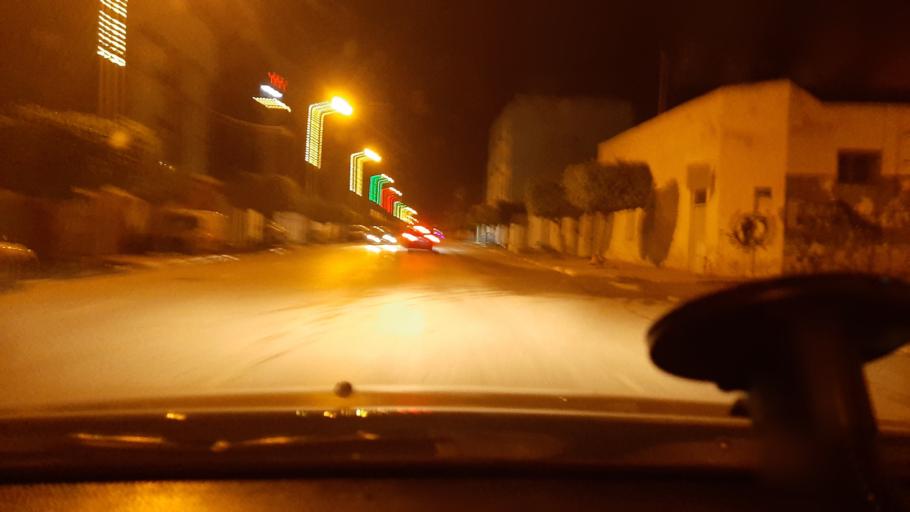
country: TN
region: Safaqis
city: Sfax
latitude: 34.7775
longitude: 10.7265
